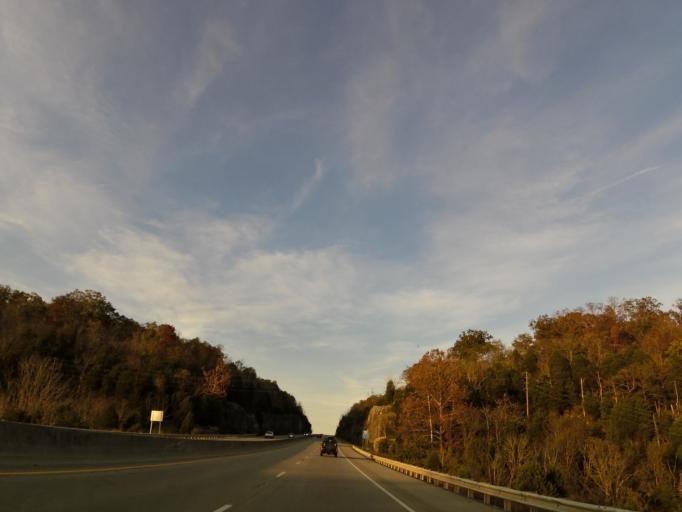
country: US
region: Kentucky
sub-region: Jessamine County
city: Wilmore
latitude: 37.7701
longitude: -84.6141
